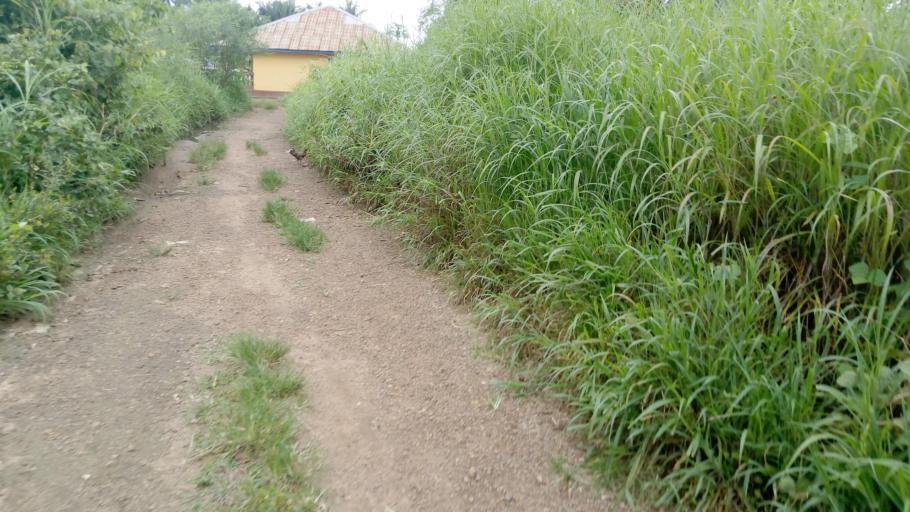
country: SL
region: Northern Province
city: Makeni
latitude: 8.8915
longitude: -12.0285
